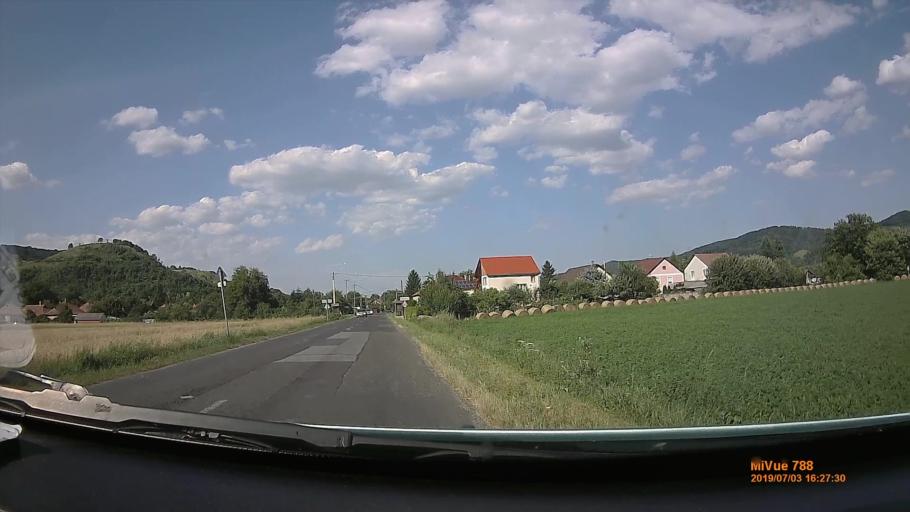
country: HU
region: Borsod-Abauj-Zemplen
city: Sajokaza
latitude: 48.2424
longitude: 20.5214
